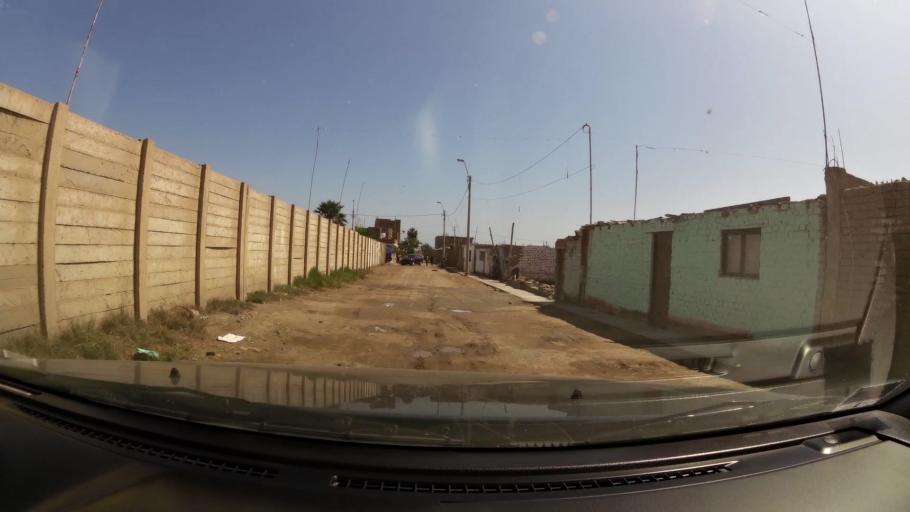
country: PE
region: Lima
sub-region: Provincia de Canete
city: San Vicente de Canete
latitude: -13.0212
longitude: -76.4784
